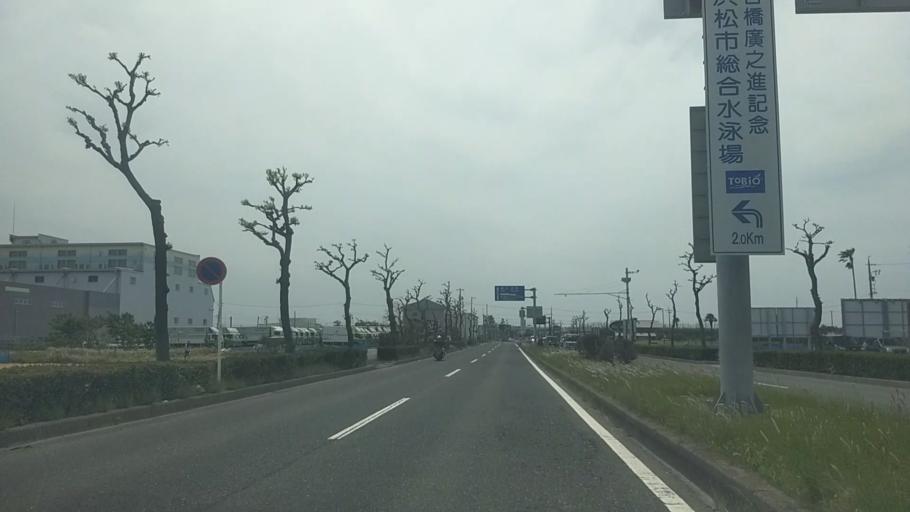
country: JP
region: Shizuoka
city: Hamamatsu
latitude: 34.6800
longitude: 137.6480
